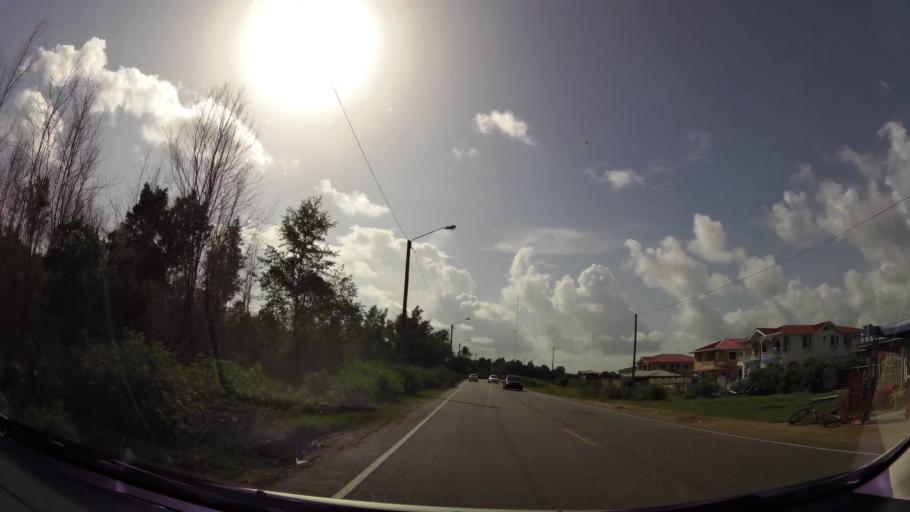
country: GY
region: Demerara-Mahaica
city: Mahaica Village
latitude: 6.7371
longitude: -57.9492
